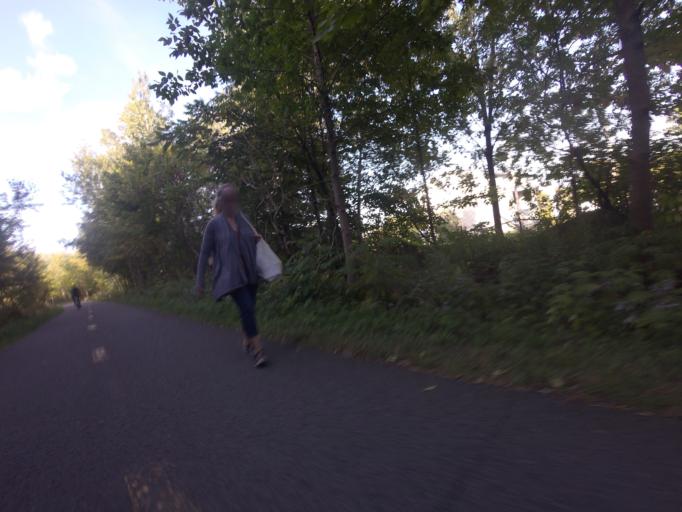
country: CA
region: Quebec
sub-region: Laurentides
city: Saint-Jerome
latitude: 45.7909
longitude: -73.9969
